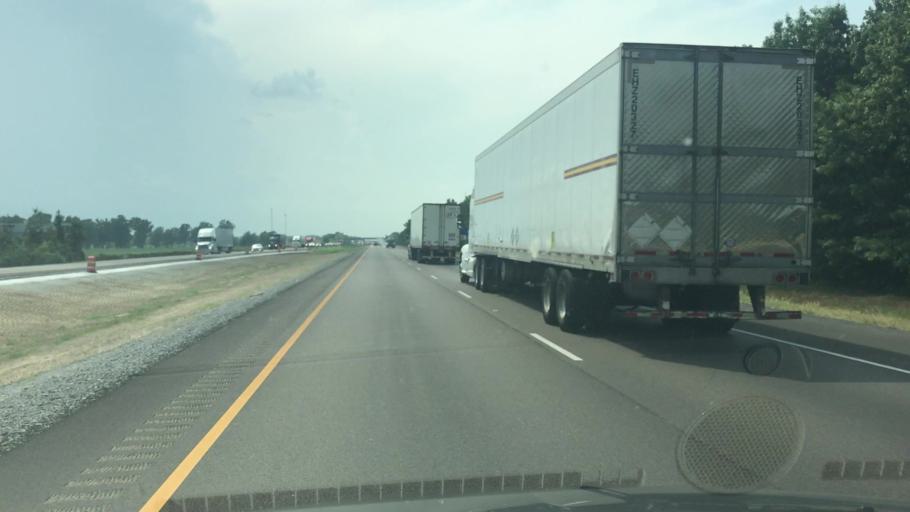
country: US
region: Arkansas
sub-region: Crittenden County
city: Earle
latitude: 35.1338
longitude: -90.4566
